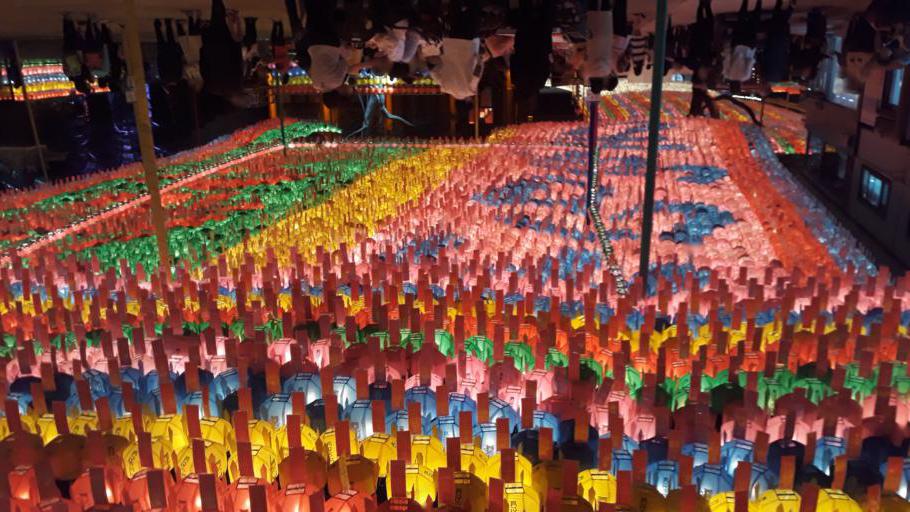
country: KR
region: Seoul
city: Seoul
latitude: 37.5728
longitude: 126.9831
